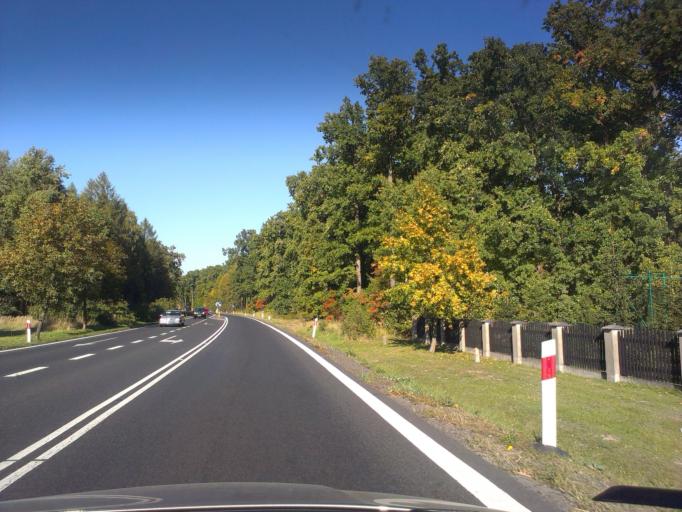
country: PL
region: Greater Poland Voivodeship
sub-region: Powiat chodzieski
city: Budzyn
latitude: 52.9093
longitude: 16.9731
